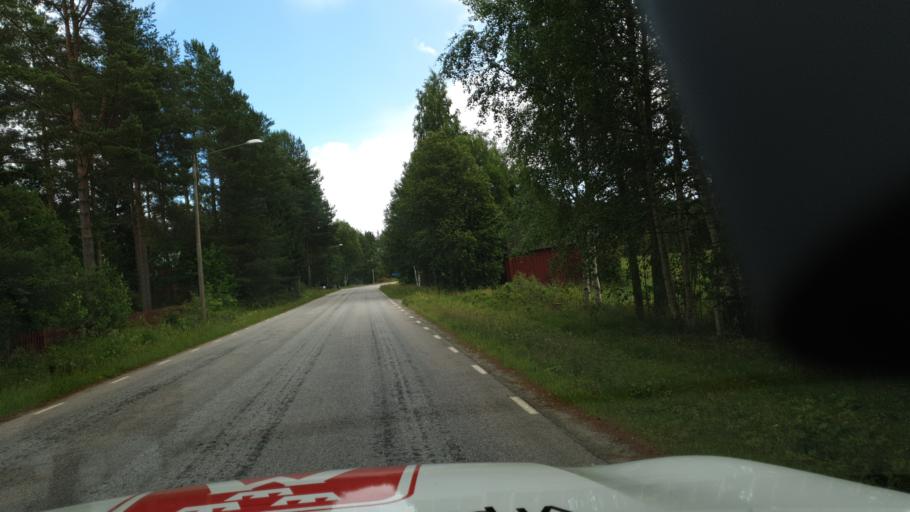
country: SE
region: Vaesterbotten
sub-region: Umea Kommun
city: Roback
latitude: 63.8471
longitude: 20.1153
